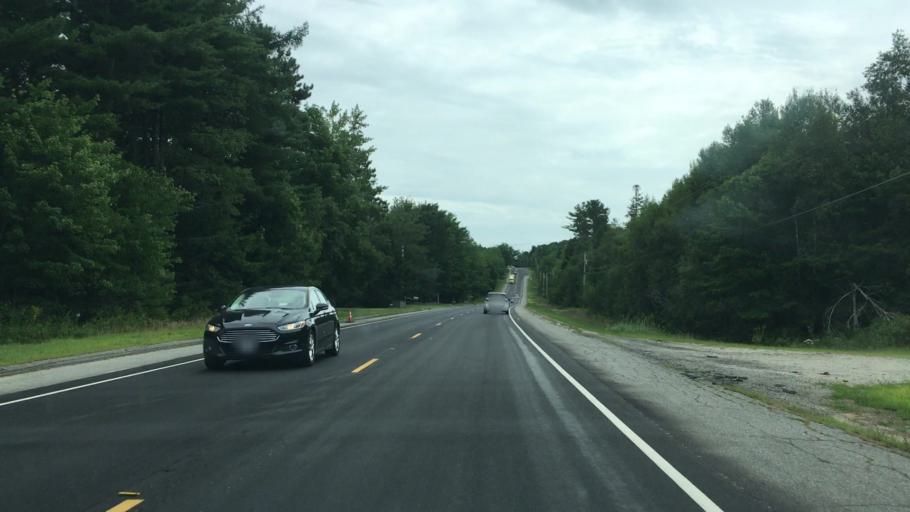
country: US
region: Maine
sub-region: Washington County
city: Addison
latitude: 44.9430
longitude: -67.7106
